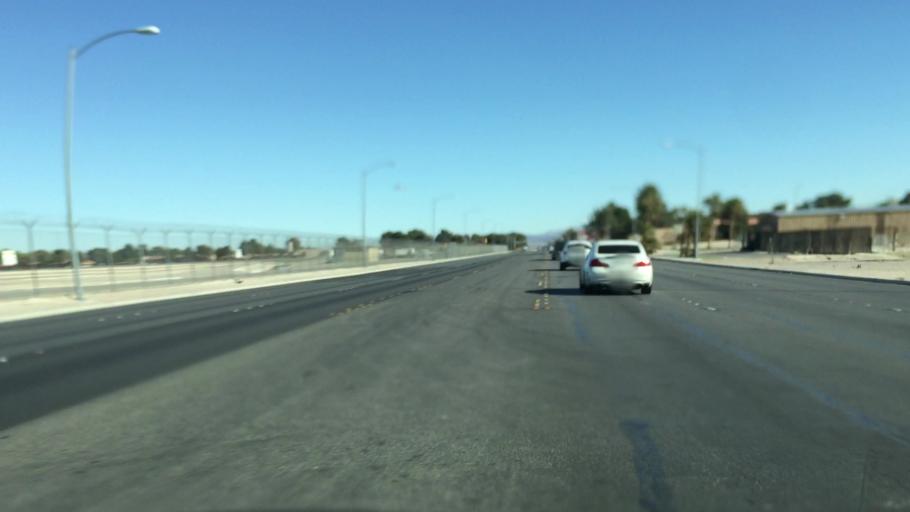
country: US
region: Nevada
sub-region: Clark County
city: Paradise
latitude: 36.0717
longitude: -115.1254
